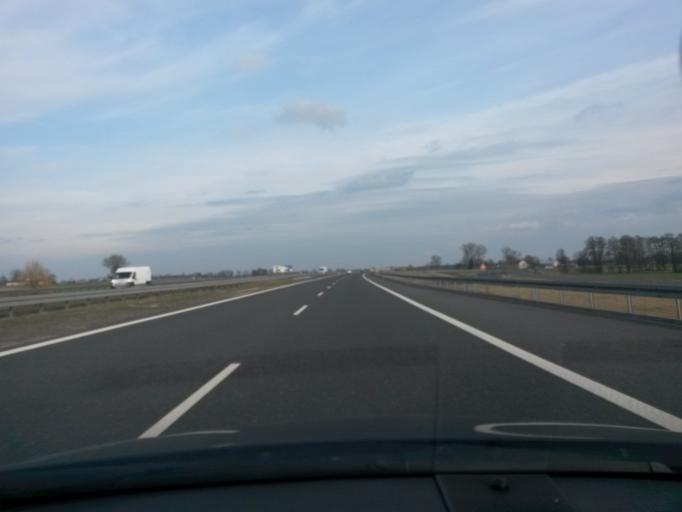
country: PL
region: Lodz Voivodeship
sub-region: Powiat poddebicki
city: Dalikow
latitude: 51.9653
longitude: 19.1111
